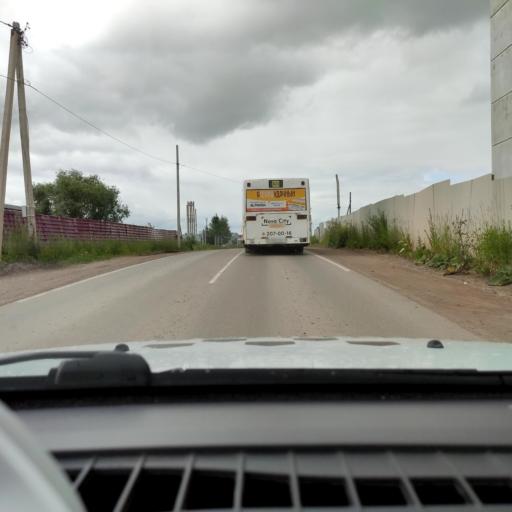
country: RU
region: Perm
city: Froly
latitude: 57.9184
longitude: 56.2831
